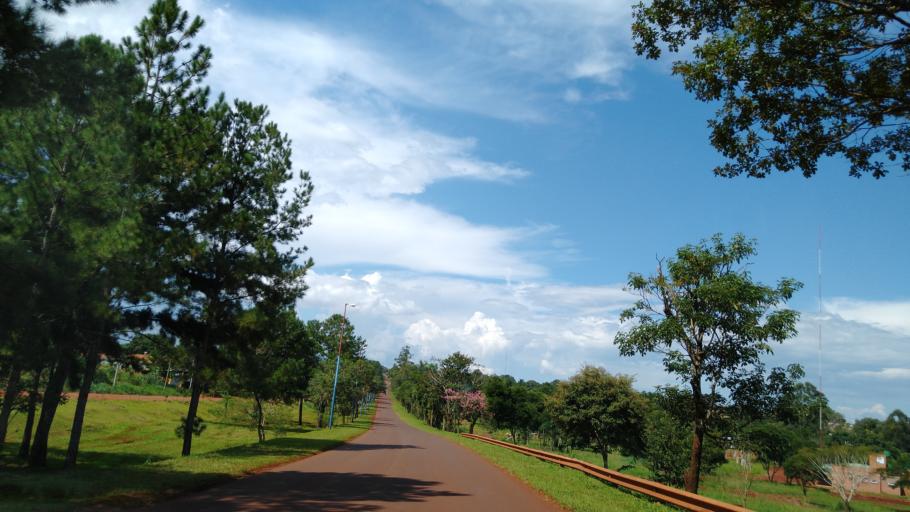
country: AR
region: Misiones
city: Puerto Libertad
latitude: -25.9705
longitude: -54.5681
